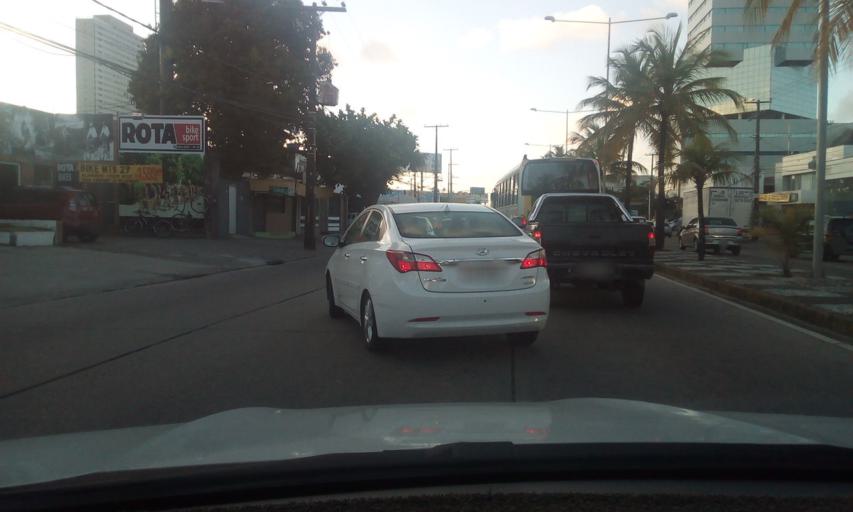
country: BR
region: Pernambuco
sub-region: Recife
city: Recife
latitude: -8.0866
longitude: -34.8856
